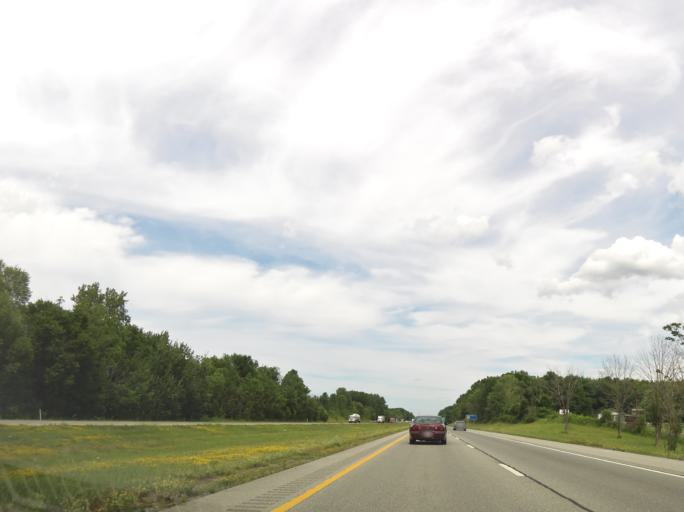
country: US
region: Ohio
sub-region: Lake County
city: Madison
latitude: 41.7489
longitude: -81.0728
